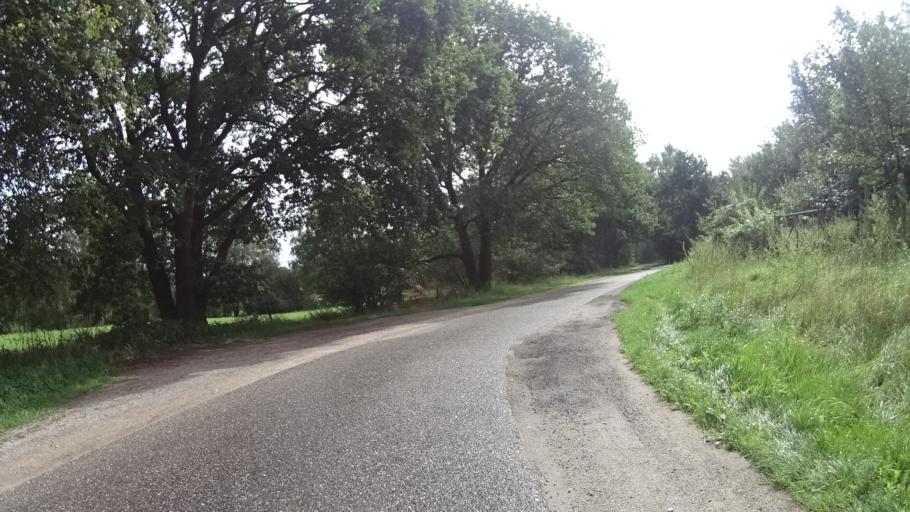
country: DE
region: Schleswig-Holstein
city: Henstedt-Ulzburg
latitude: 53.7589
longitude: 10.0123
